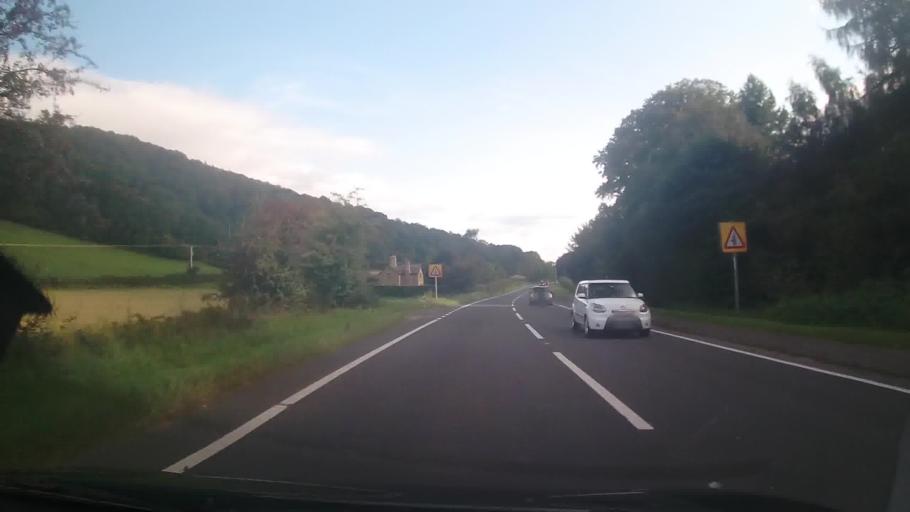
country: GB
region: England
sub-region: Shropshire
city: Craven Arms
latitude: 52.4310
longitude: -2.8270
